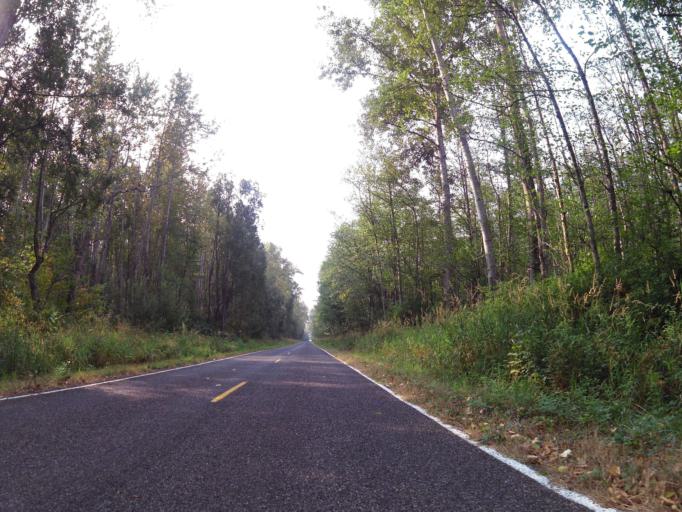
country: US
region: Washington
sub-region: Whatcom County
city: Birch Bay
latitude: 48.8681
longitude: -122.7318
